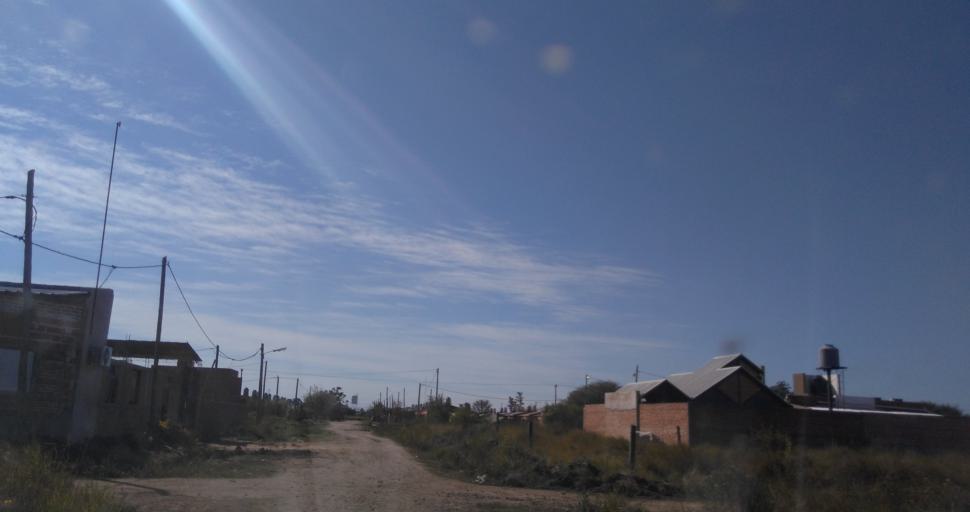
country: AR
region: Chaco
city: Fontana
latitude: -27.4590
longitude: -59.0453
